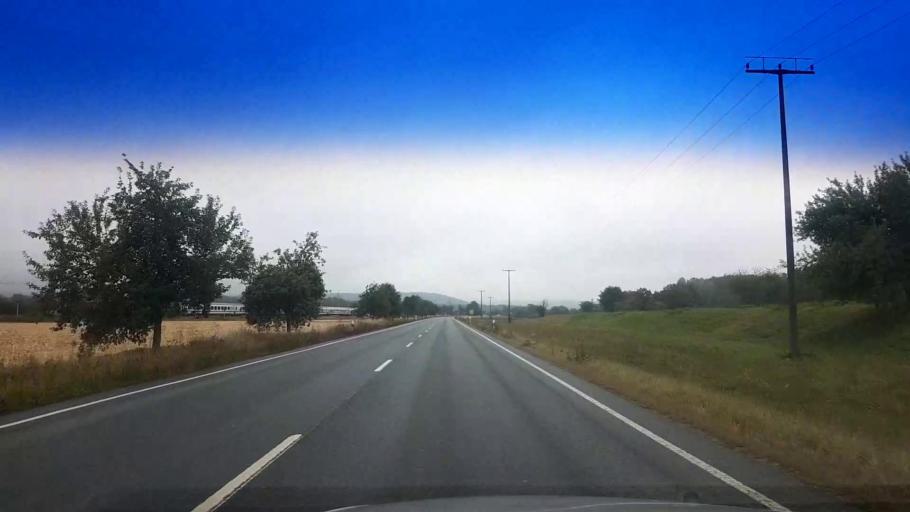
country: DE
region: Bavaria
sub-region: Upper Franconia
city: Eggolsheim
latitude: 49.7606
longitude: 11.0482
